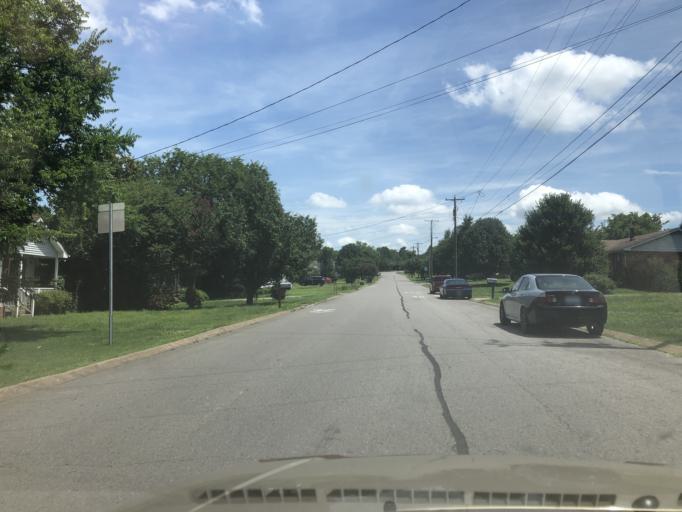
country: US
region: Tennessee
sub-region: Davidson County
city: Lakewood
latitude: 36.2476
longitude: -86.6814
